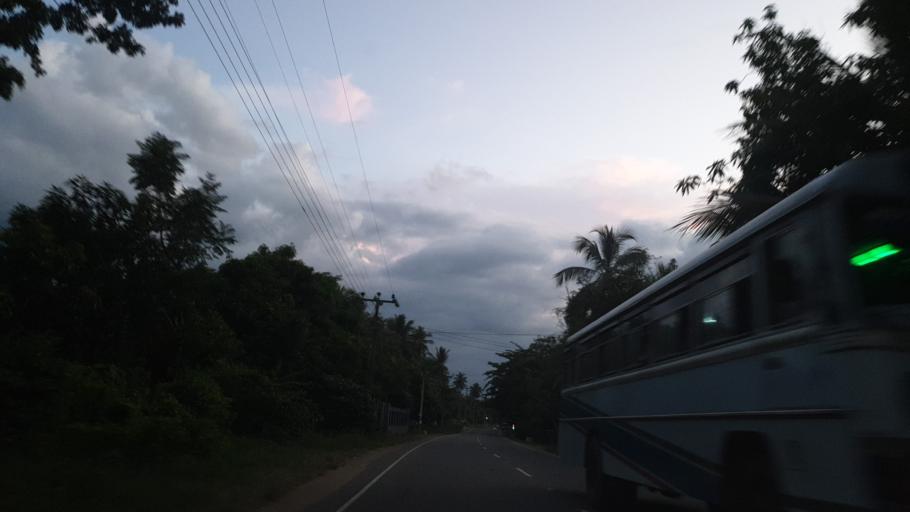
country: LK
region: North Western
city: Kurunegala
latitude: 7.5854
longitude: 80.2001
